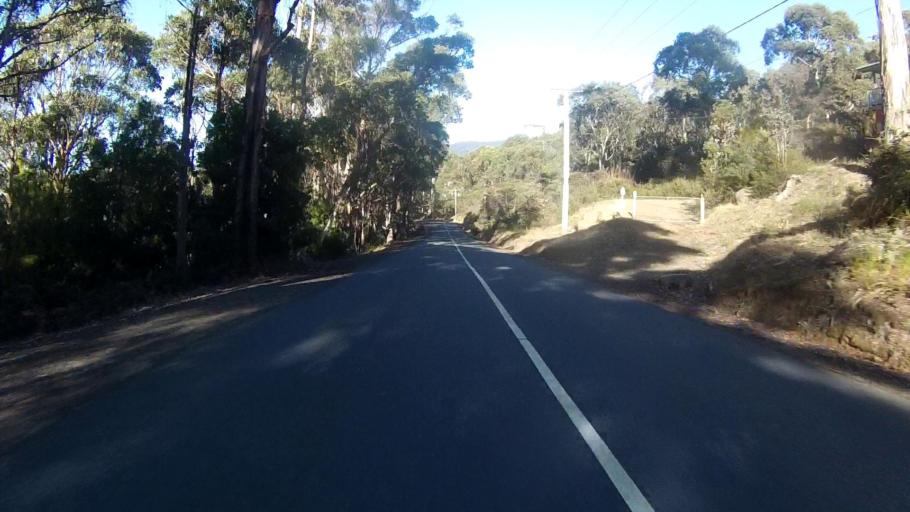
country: AU
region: Tasmania
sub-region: Clarence
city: Sandford
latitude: -43.0298
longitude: 147.9273
